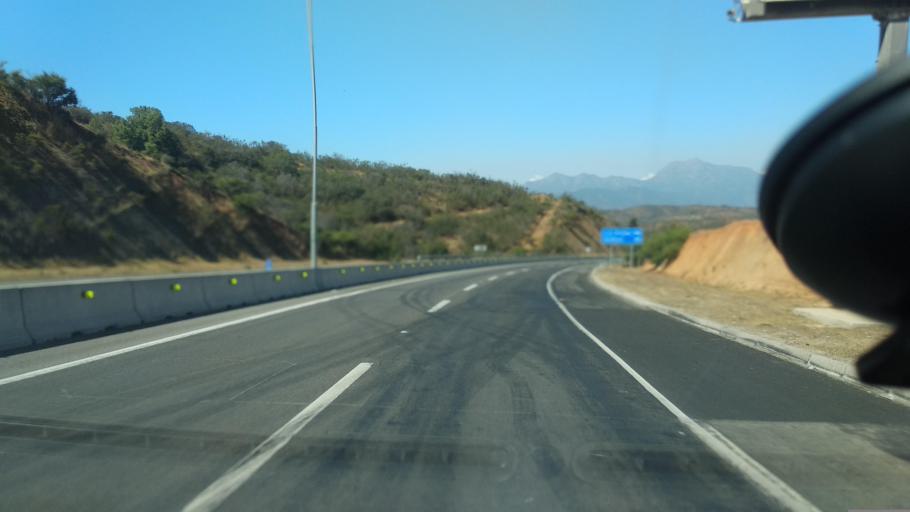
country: CL
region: Valparaiso
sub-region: Provincia de Marga Marga
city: Villa Alemana
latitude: -33.0455
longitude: -71.3242
